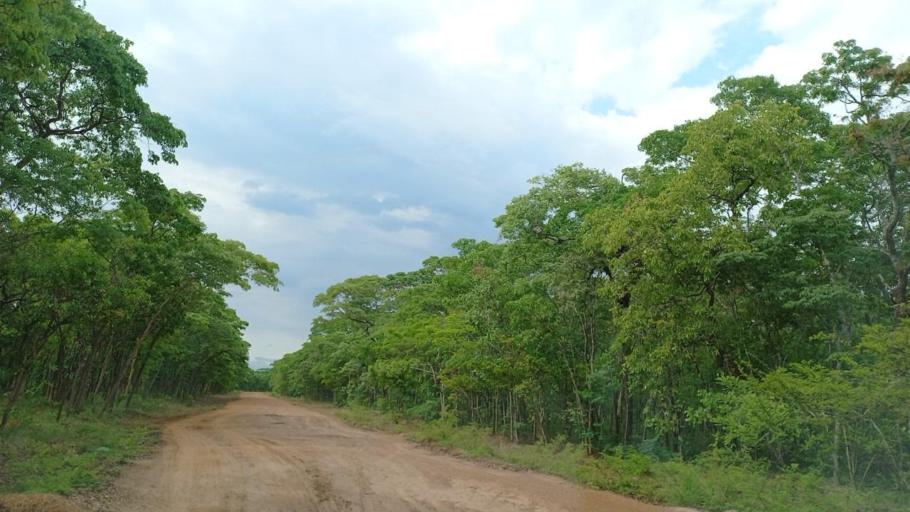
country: ZM
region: North-Western
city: Kalengwa
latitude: -13.3888
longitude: 25.0707
